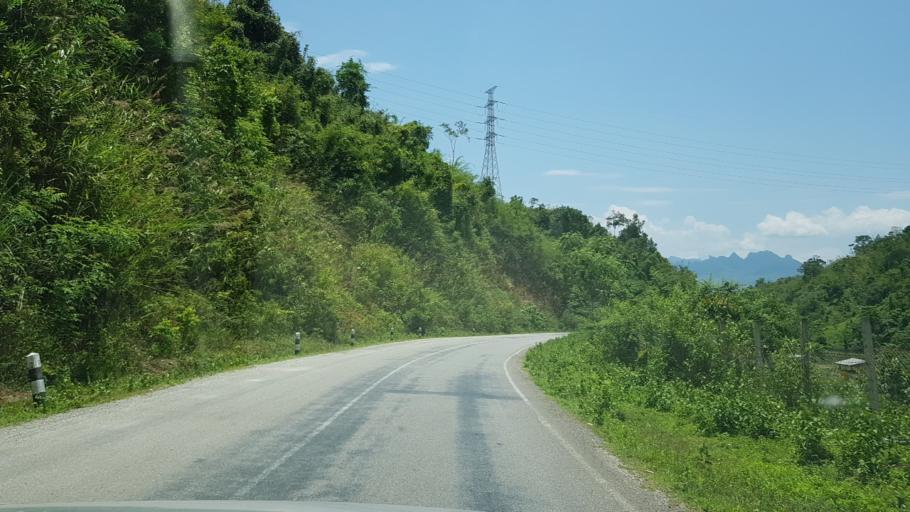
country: LA
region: Vientiane
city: Muang Kasi
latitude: 19.2713
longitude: 102.2091
